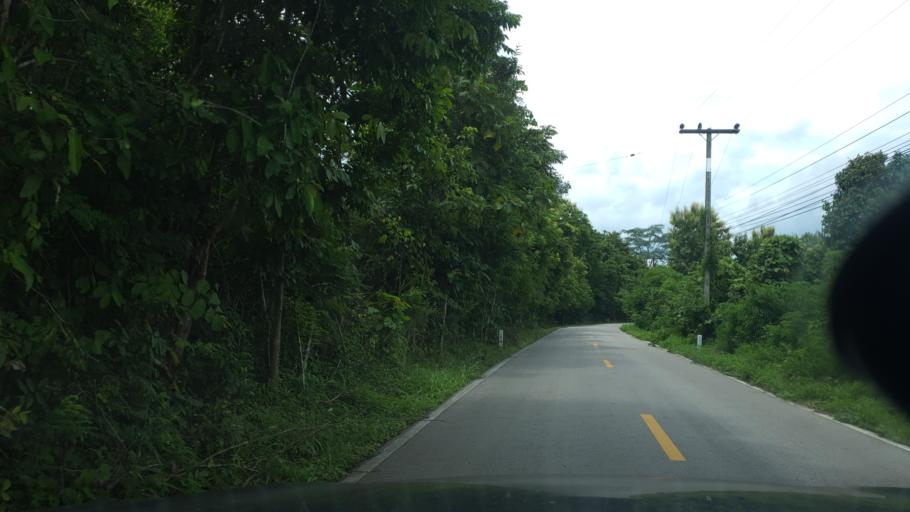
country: TH
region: Lampang
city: Hang Chat
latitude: 18.3917
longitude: 99.2643
